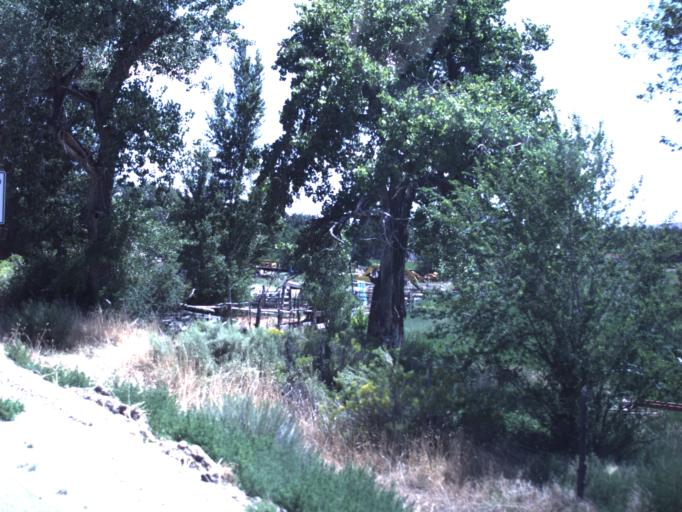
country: US
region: Utah
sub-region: Emery County
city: Orangeville
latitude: 39.2380
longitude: -111.0552
